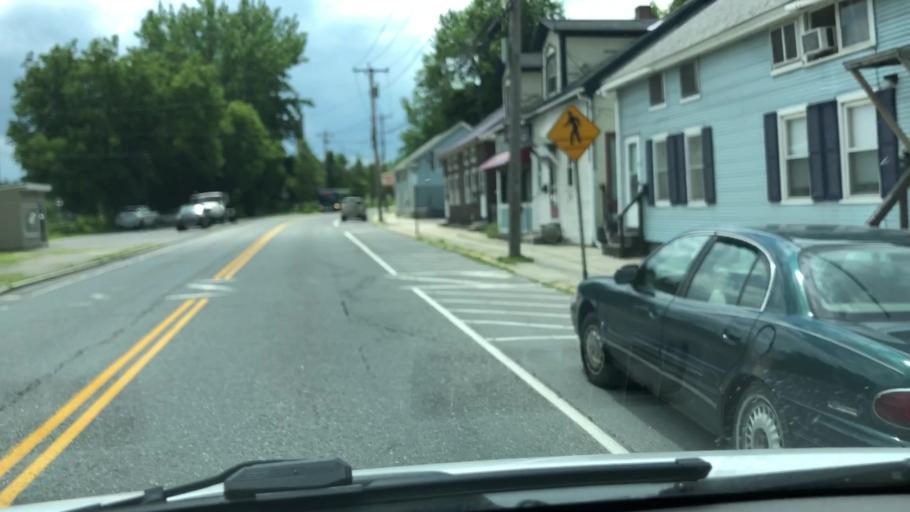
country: US
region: Massachusetts
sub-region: Berkshire County
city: Adams
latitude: 42.6290
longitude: -73.1158
